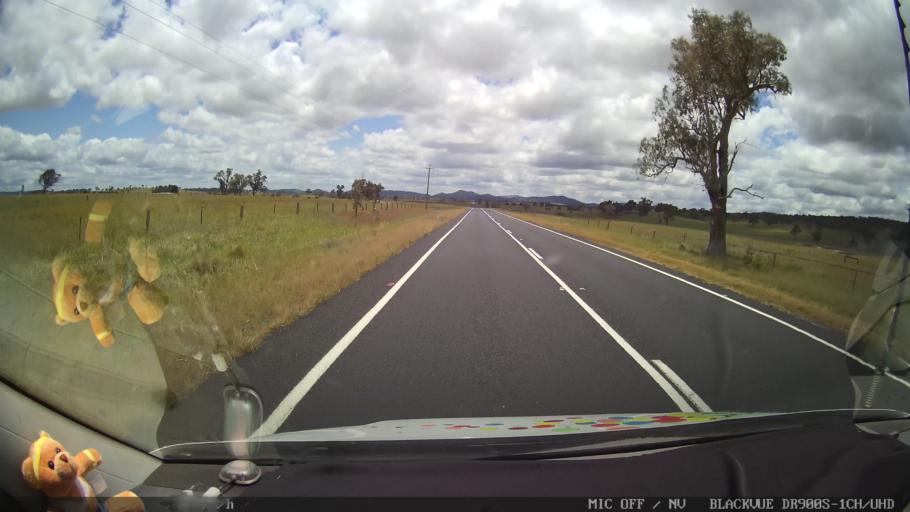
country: AU
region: New South Wales
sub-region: Glen Innes Severn
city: Glen Innes
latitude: -29.4242
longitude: 151.8592
